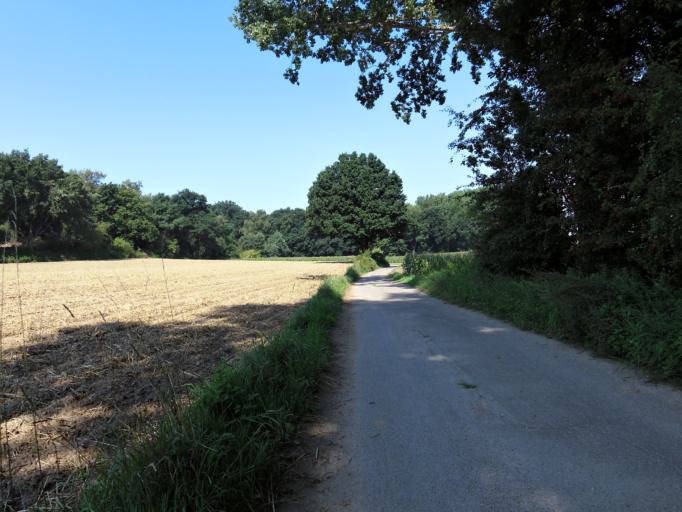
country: DE
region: North Rhine-Westphalia
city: Huckelhoven
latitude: 51.0187
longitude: 6.2072
